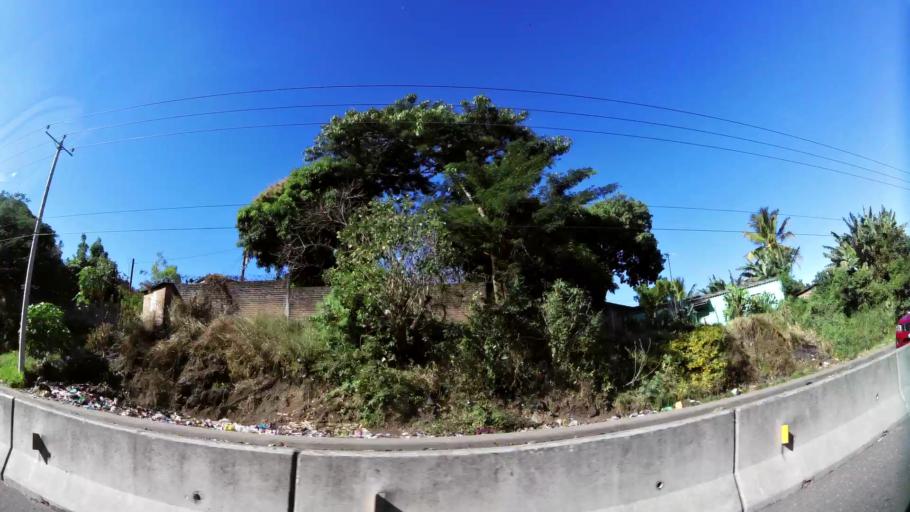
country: SV
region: Santa Ana
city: Santa Ana
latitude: 13.9697
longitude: -89.5830
